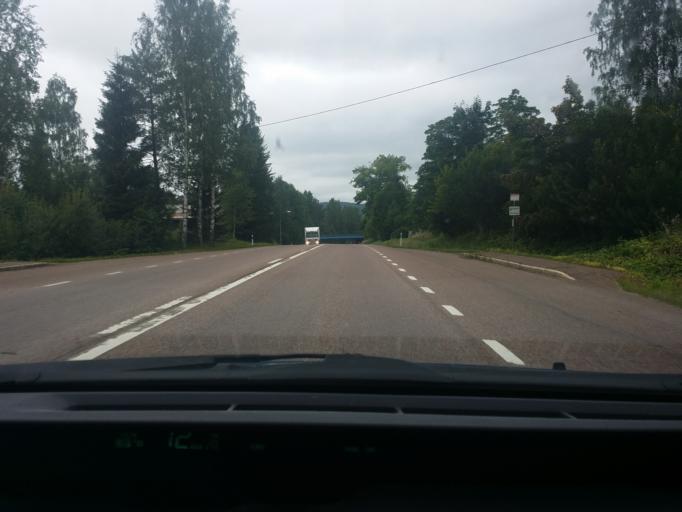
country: SE
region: Dalarna
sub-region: Gagnefs Kommun
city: Djuras
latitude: 60.5390
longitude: 15.2848
